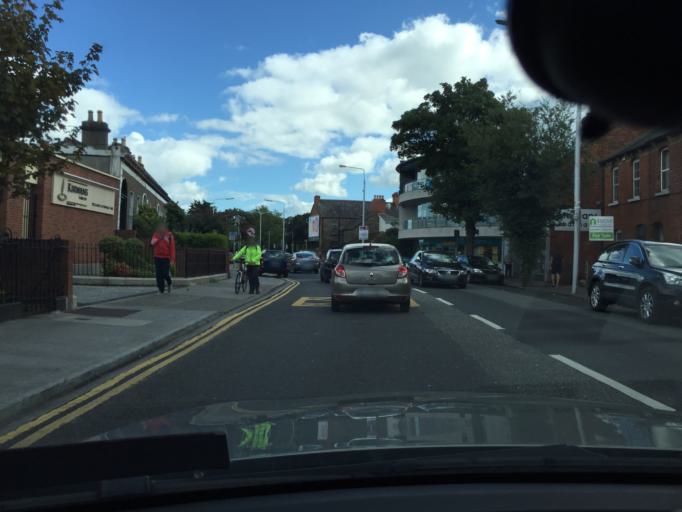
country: IE
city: Fairview
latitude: 53.3627
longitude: -6.2384
